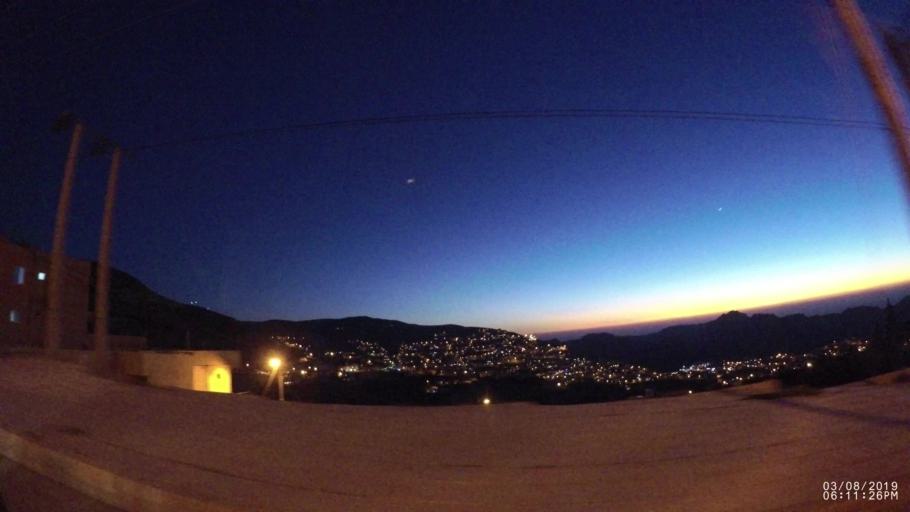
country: JO
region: Ma'an
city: Petra
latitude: 30.3292
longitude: 35.4900
